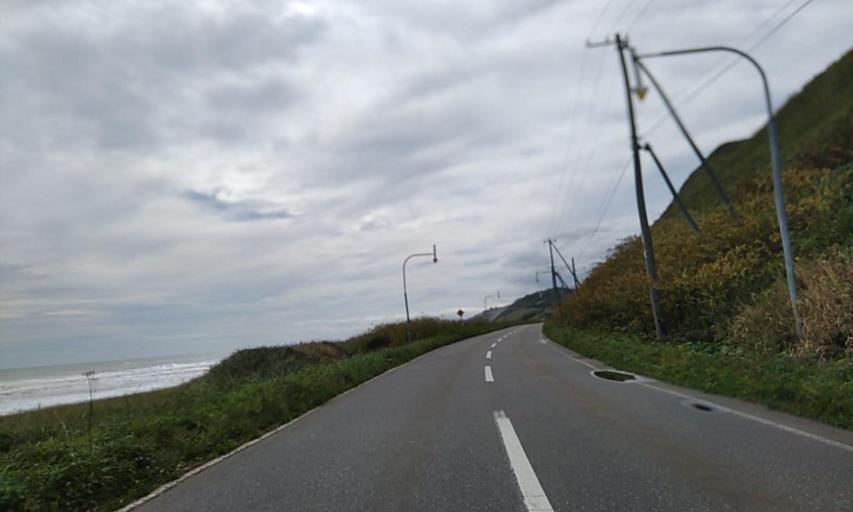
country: JP
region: Hokkaido
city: Obihiro
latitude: 42.7891
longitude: 143.7948
